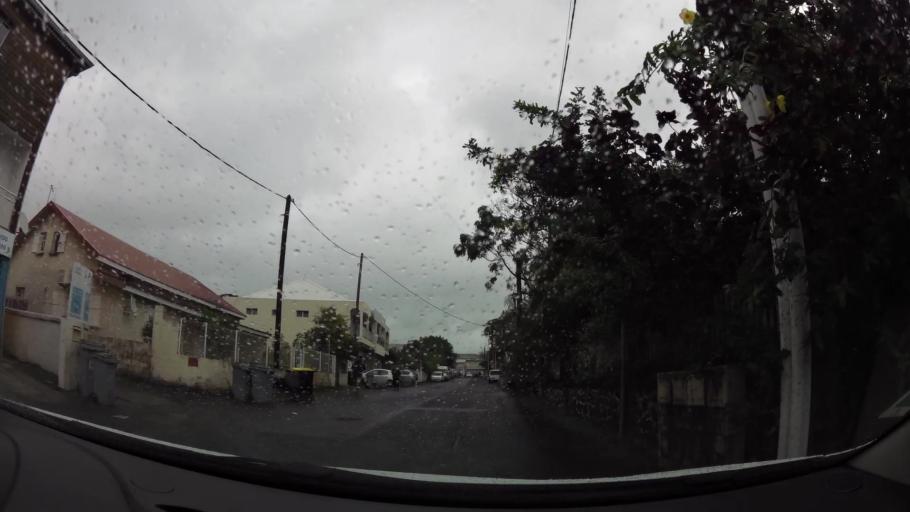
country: RE
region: Reunion
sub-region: Reunion
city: Saint-Andre
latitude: -20.9569
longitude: 55.6518
